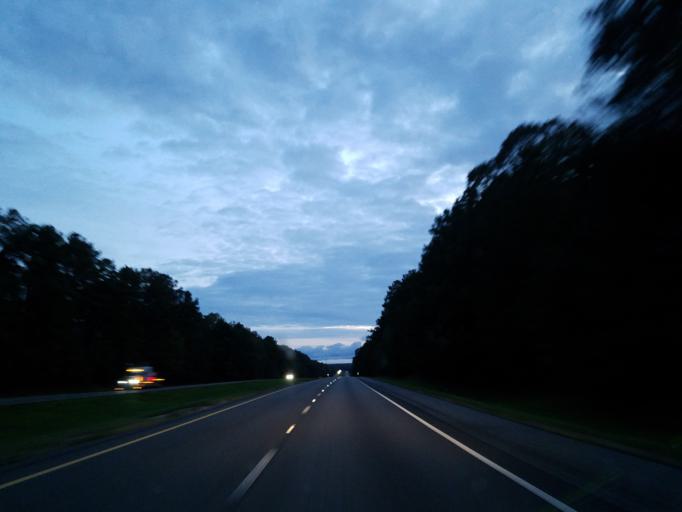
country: US
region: Mississippi
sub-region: Clarke County
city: Stonewall
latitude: 32.1192
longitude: -88.8784
